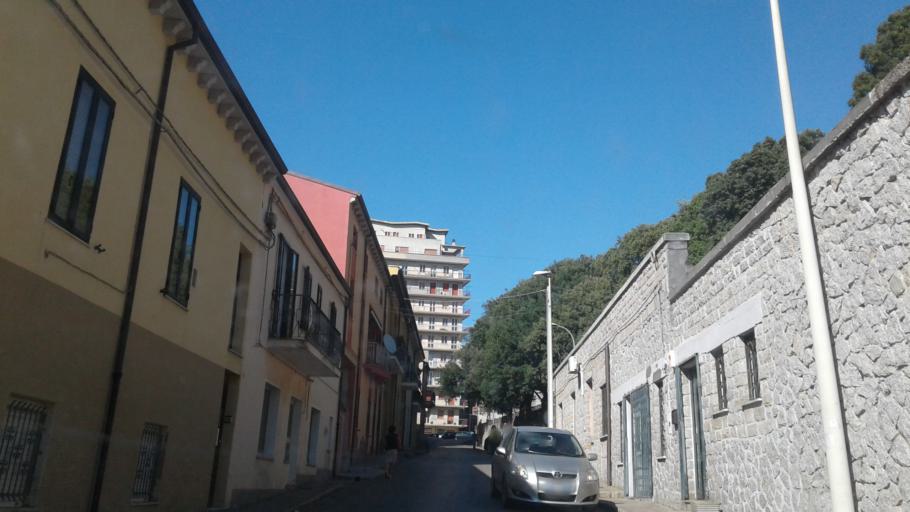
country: IT
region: Sardinia
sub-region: Provincia di Olbia-Tempio
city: Tempio Pausania
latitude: 40.9005
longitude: 9.1003
